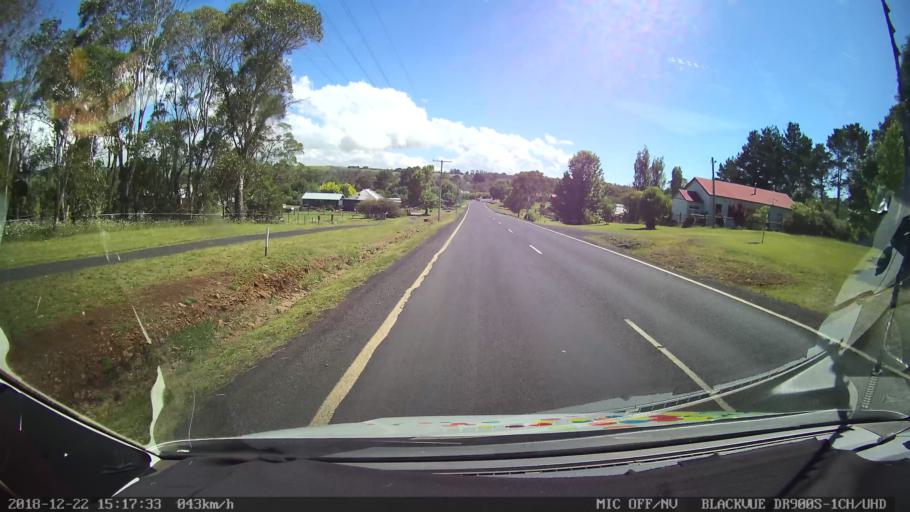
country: AU
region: New South Wales
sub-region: Bellingen
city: Dorrigo
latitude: -30.3985
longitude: 152.3522
